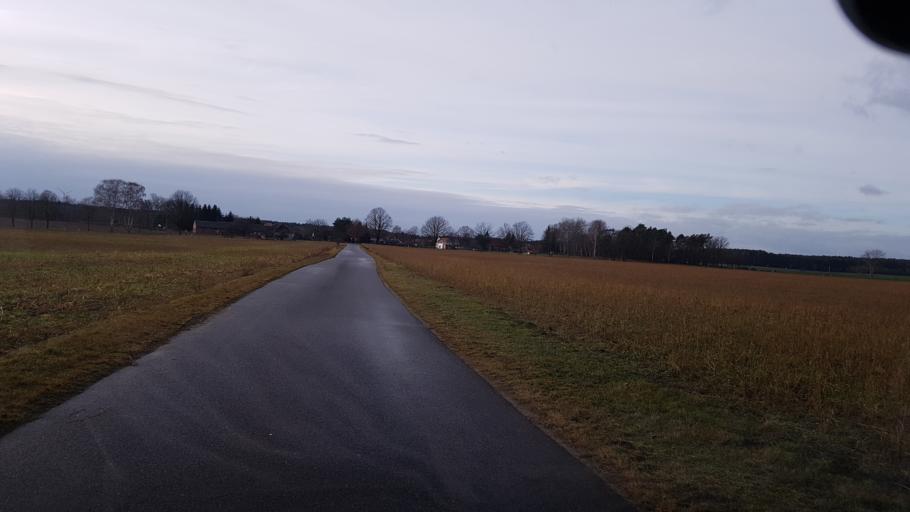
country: DE
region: Brandenburg
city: Bronkow
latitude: 51.6664
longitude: 13.8691
